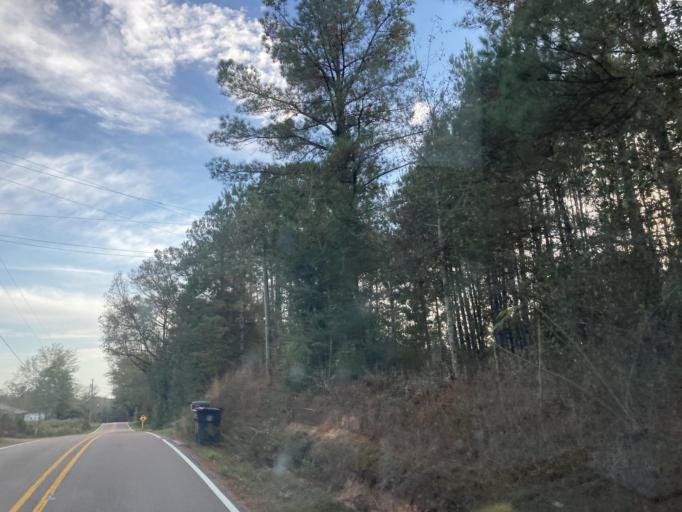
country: US
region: Mississippi
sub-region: Lamar County
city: Purvis
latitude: 31.1891
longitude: -89.3639
